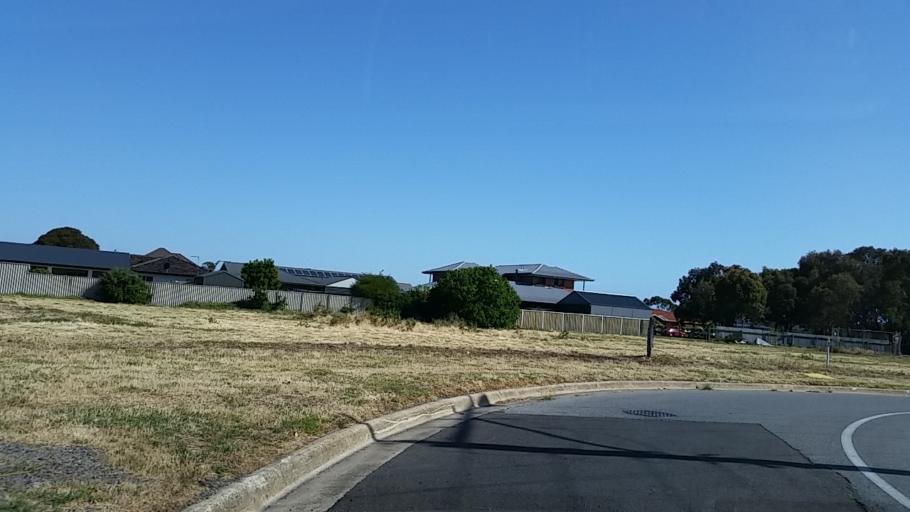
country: AU
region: South Australia
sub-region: Charles Sturt
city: Seaton
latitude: -34.9164
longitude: 138.5117
